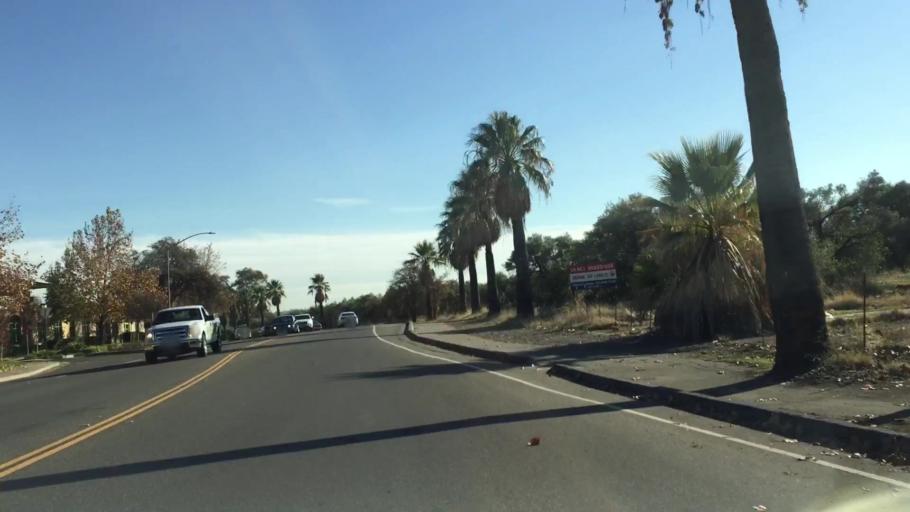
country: US
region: California
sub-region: Butte County
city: Oroville
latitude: 39.5216
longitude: -121.5551
